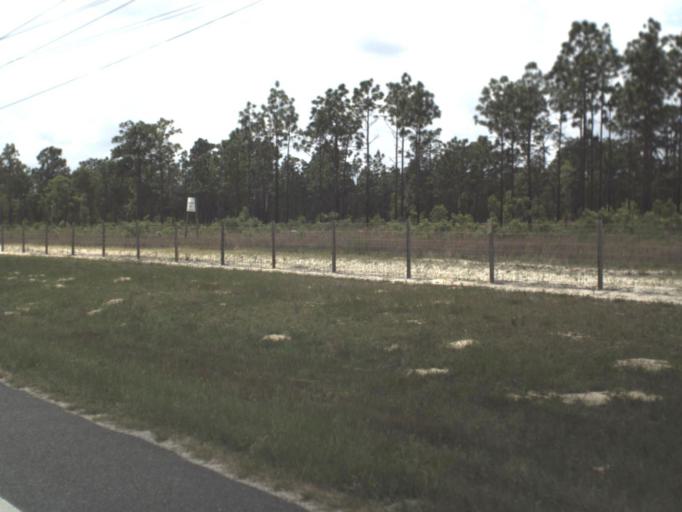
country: US
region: Florida
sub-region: Clay County
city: Keystone Heights
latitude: 29.8267
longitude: -81.9880
